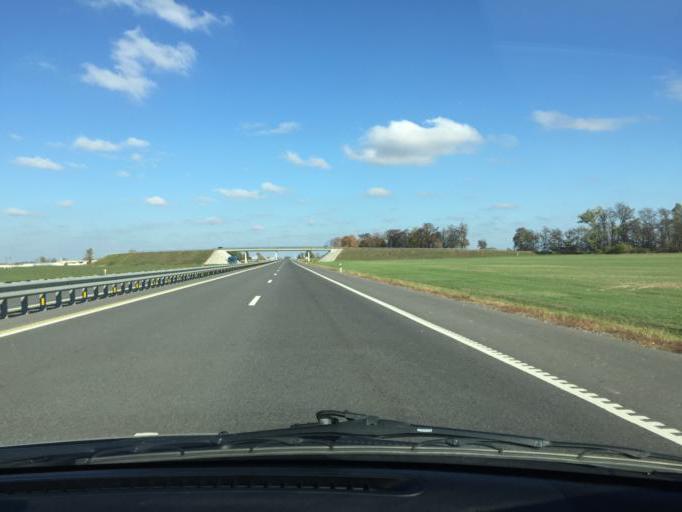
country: BY
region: Minsk
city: Slutsk
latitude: 53.0645
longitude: 27.5495
